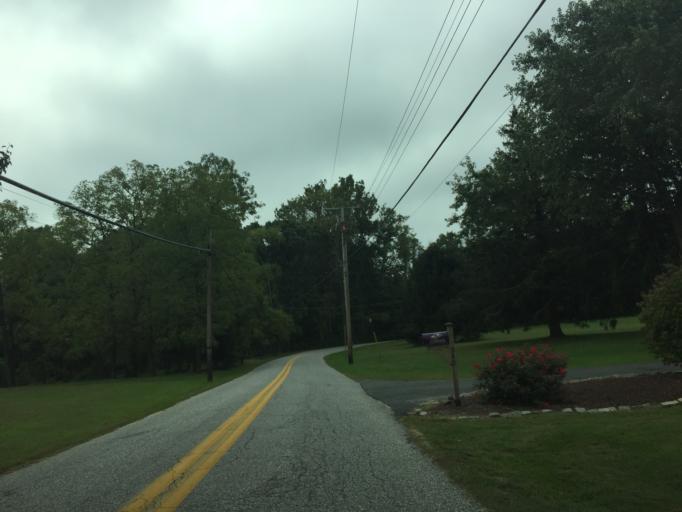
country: US
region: Maryland
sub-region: Baltimore County
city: Bowleys Quarters
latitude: 39.3724
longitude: -76.3898
